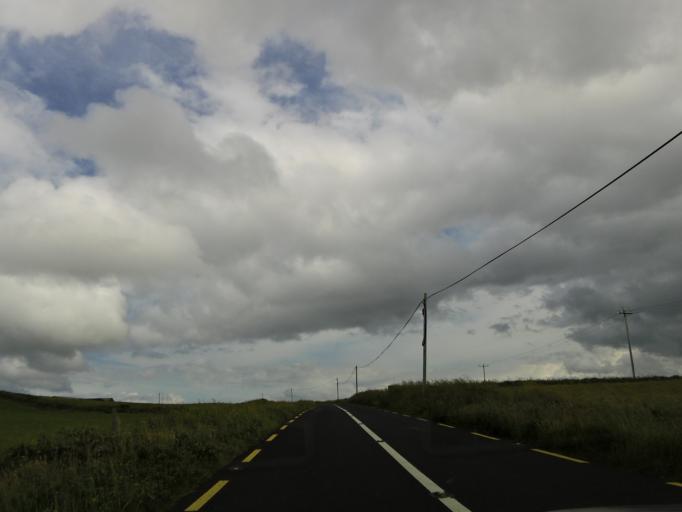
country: IE
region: Munster
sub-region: An Clar
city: Kilrush
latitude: 52.6995
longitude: -9.6251
